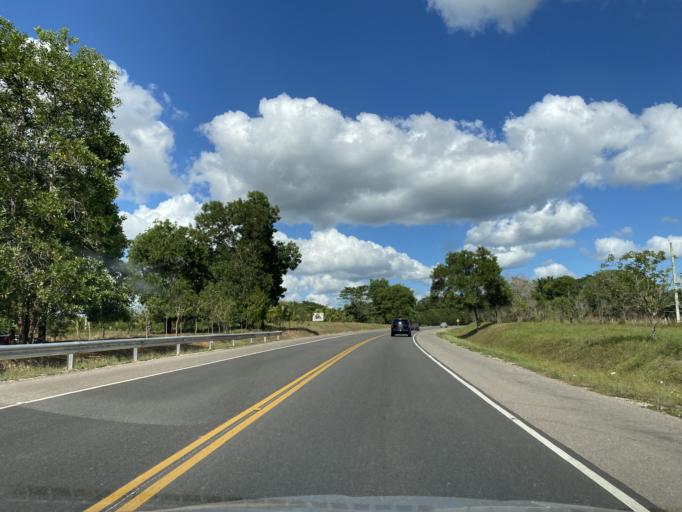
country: DO
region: Monte Plata
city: Monte Plata
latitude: 18.7586
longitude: -69.7643
